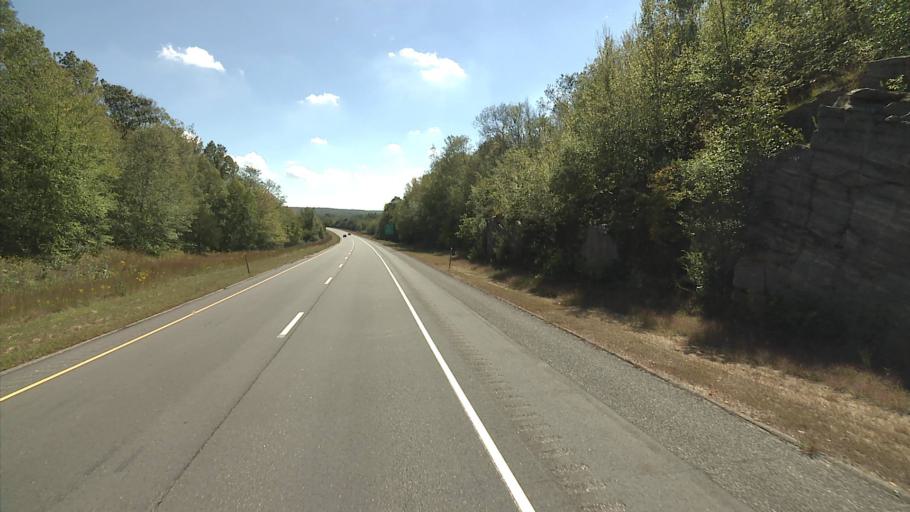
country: US
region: Connecticut
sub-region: New London County
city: Colchester
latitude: 41.4791
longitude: -72.2980
